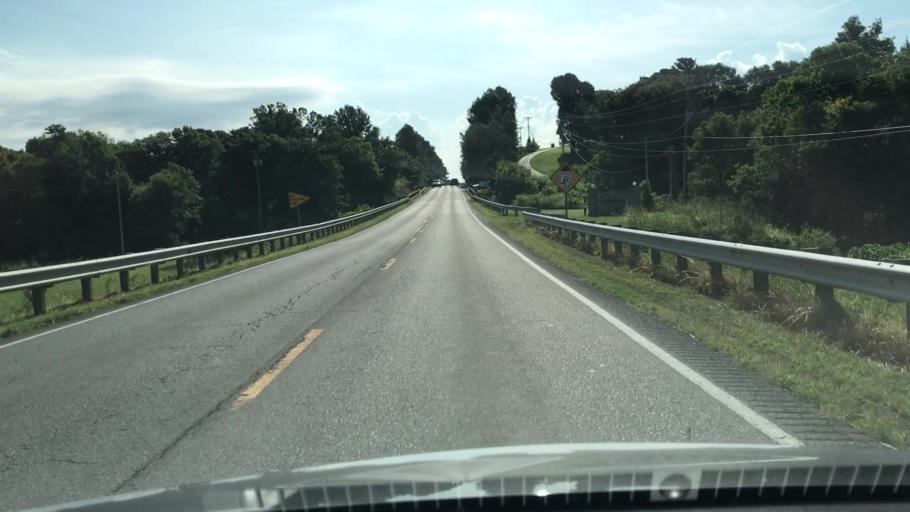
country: US
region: Kentucky
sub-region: Metcalfe County
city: Edmonton
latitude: 36.9886
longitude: -85.6457
